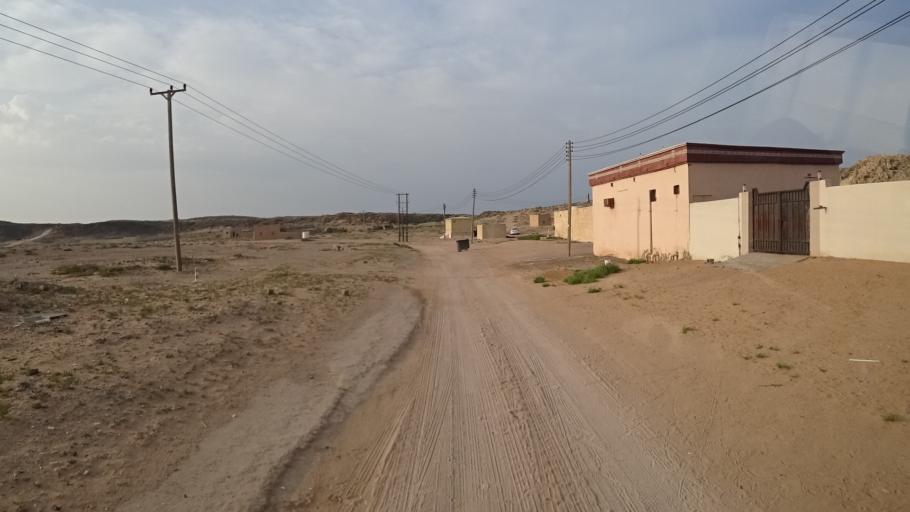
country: OM
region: Ash Sharqiyah
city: Sur
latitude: 22.4482
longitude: 59.8273
